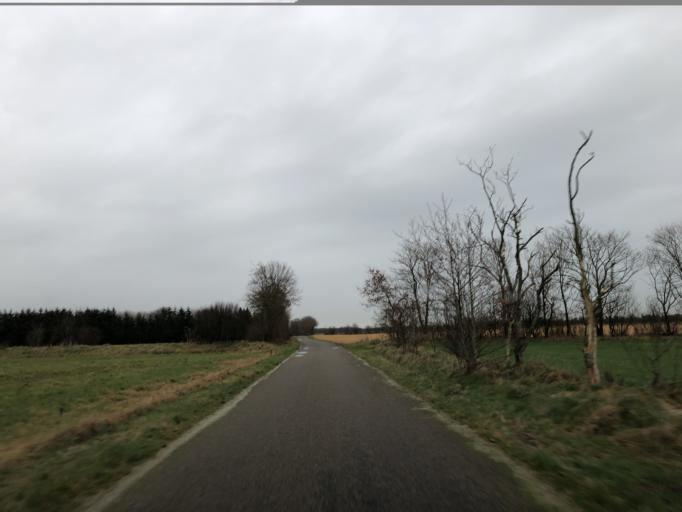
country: DK
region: Central Jutland
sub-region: Holstebro Kommune
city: Vinderup
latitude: 56.3765
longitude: 8.8549
